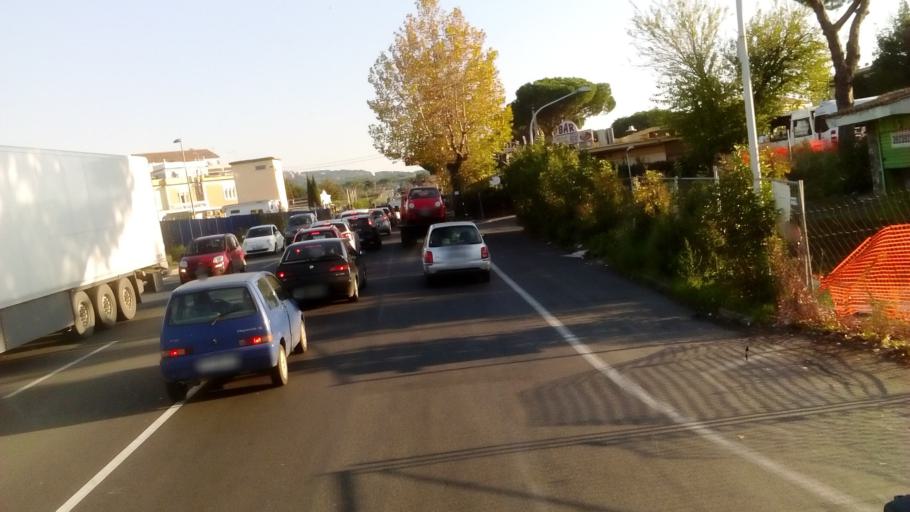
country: IT
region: Latium
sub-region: Citta metropolitana di Roma Capitale
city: Marino
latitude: 41.7680
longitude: 12.6153
